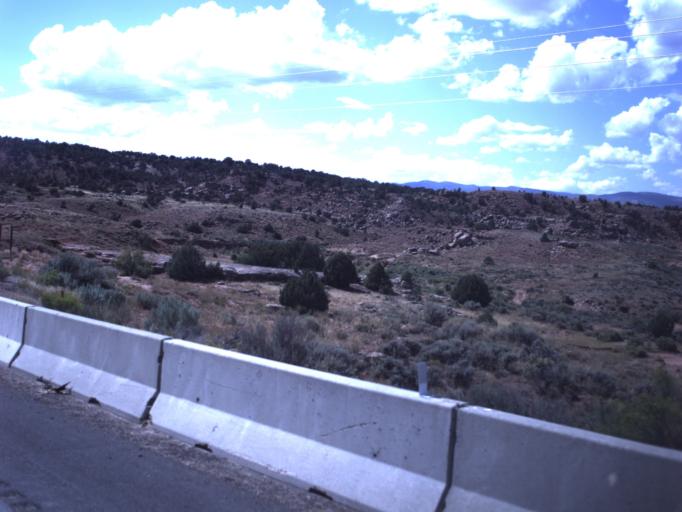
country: US
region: Utah
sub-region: Duchesne County
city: Duchesne
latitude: 40.2105
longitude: -110.7589
